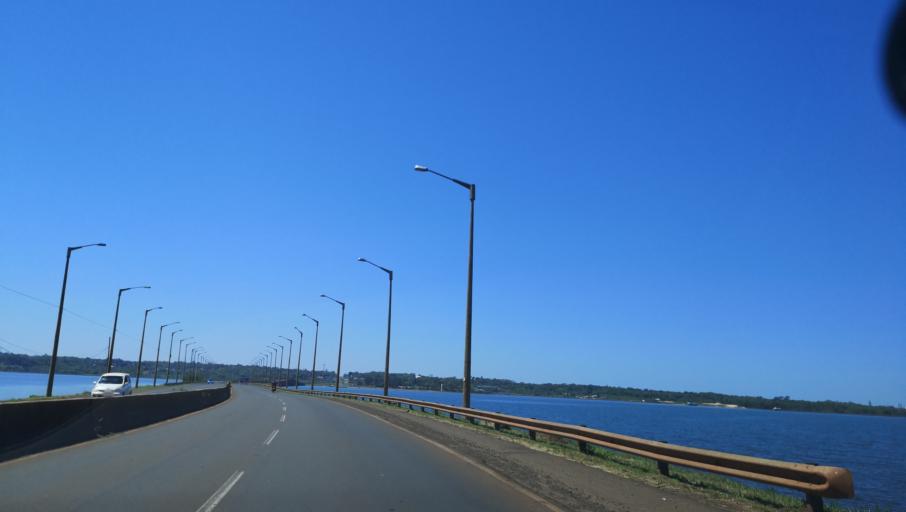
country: PY
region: Itapua
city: San Juan del Parana
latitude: -27.2945
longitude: -55.9104
